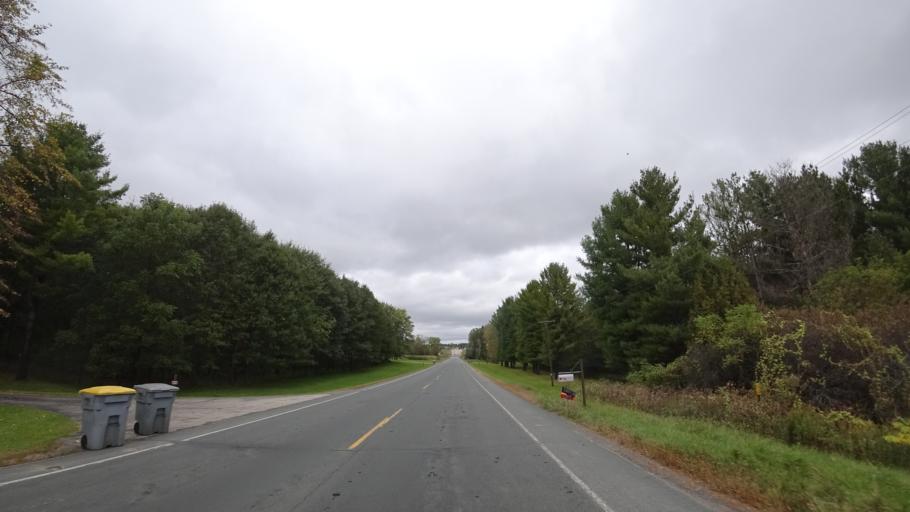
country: US
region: Wisconsin
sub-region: Saint Croix County
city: Woodville
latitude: 44.9271
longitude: -92.2783
